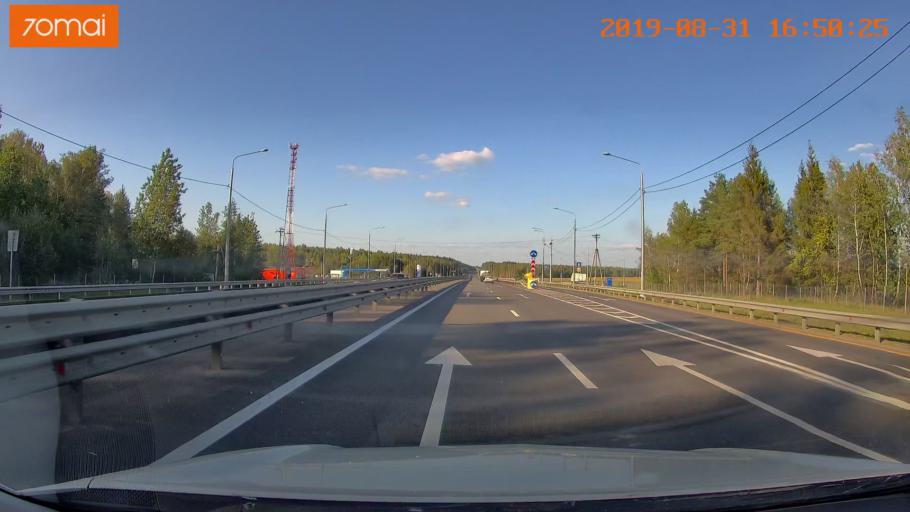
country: RU
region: Kaluga
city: Pyatovskiy
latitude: 54.7083
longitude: 36.1625
